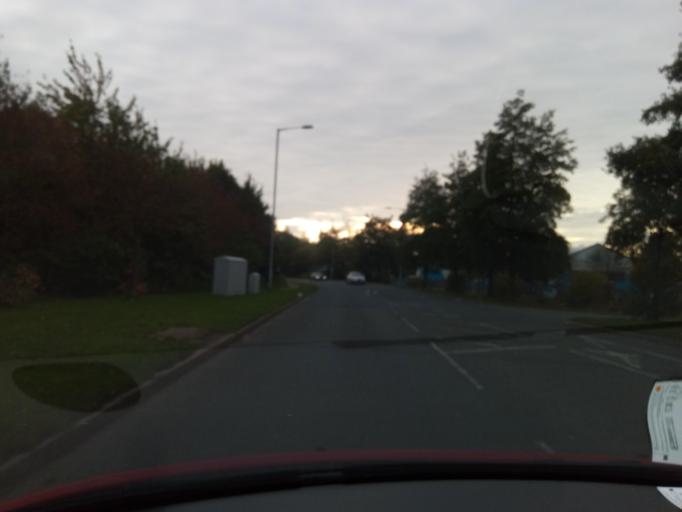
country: GB
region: England
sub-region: County Durham
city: Shildon
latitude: 54.6244
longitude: -1.6479
